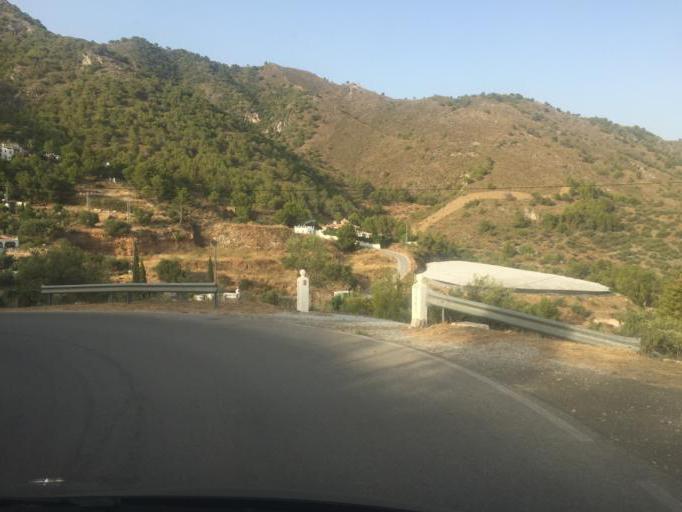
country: ES
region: Andalusia
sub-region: Provincia de Malaga
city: Frigiliana
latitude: 36.8036
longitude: -3.9170
